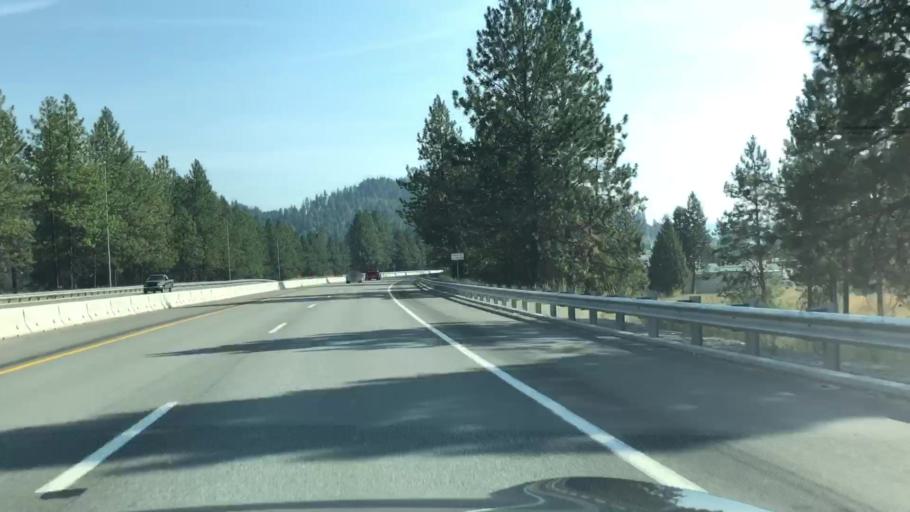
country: US
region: Idaho
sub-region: Kootenai County
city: Coeur d'Alene
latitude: 47.6771
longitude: -116.7536
